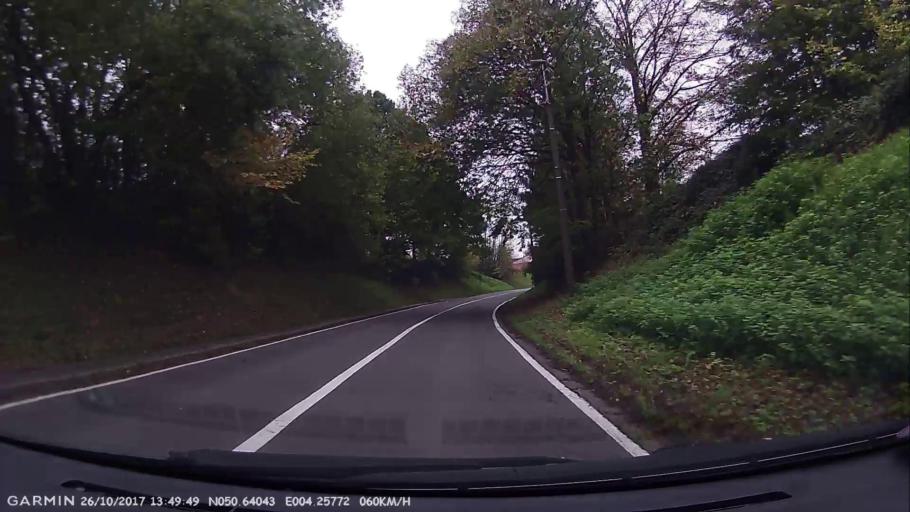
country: BE
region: Wallonia
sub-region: Province du Brabant Wallon
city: Ittre
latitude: 50.6403
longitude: 4.2577
